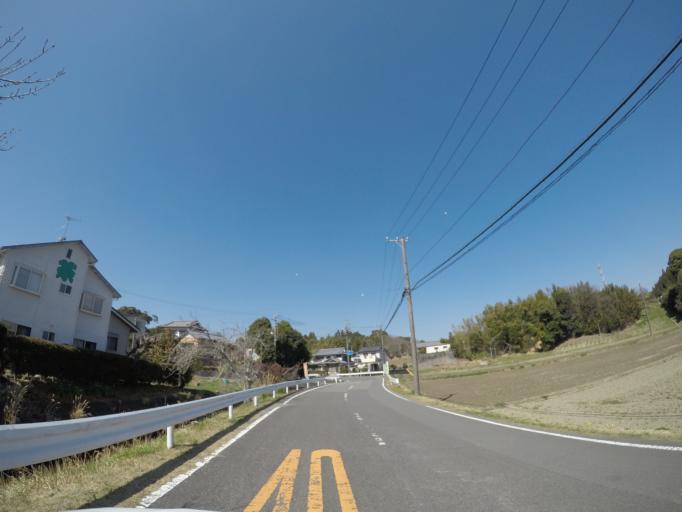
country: JP
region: Shizuoka
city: Kanaya
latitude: 34.7820
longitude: 138.1090
